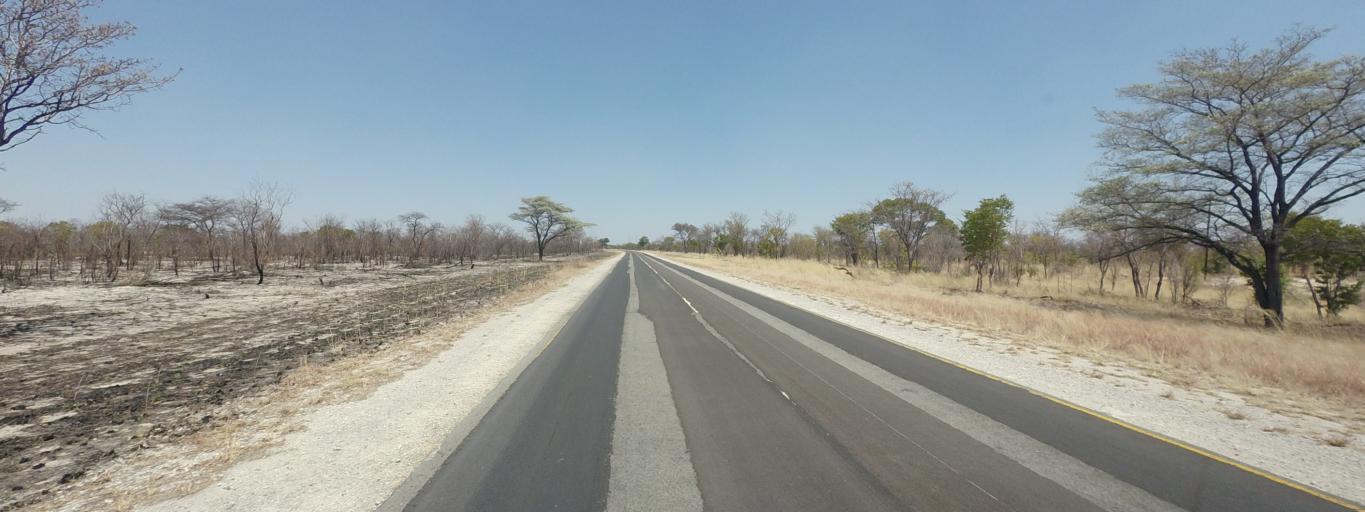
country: BW
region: North West
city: Shakawe
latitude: -18.0393
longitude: 21.9734
